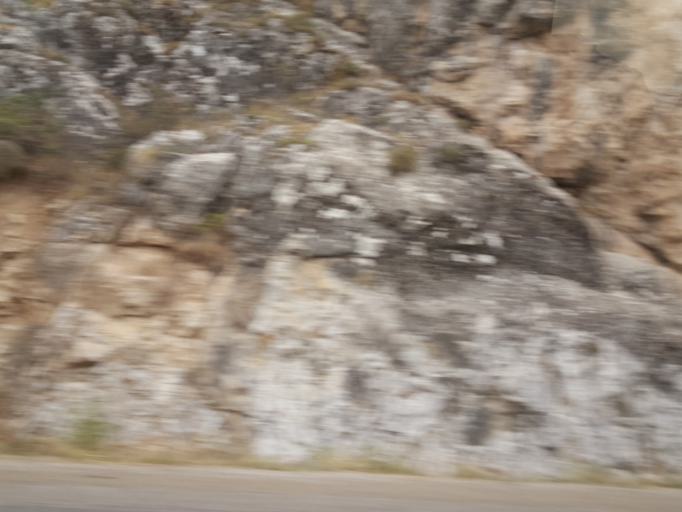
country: TR
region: Yozgat
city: Cekerek
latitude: 40.2039
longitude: 35.4689
